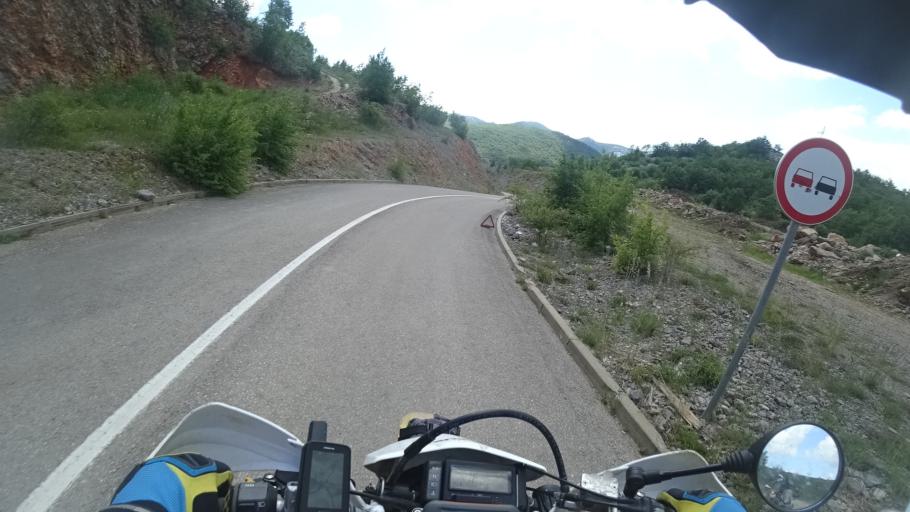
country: HR
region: Zadarska
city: Gracac
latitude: 44.2768
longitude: 15.9339
